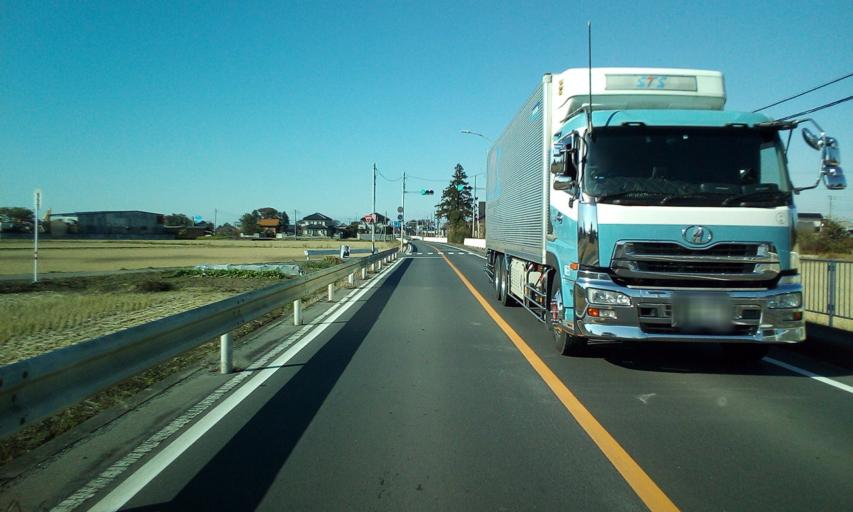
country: JP
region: Saitama
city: Sugito
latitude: 36.0512
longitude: 139.7762
